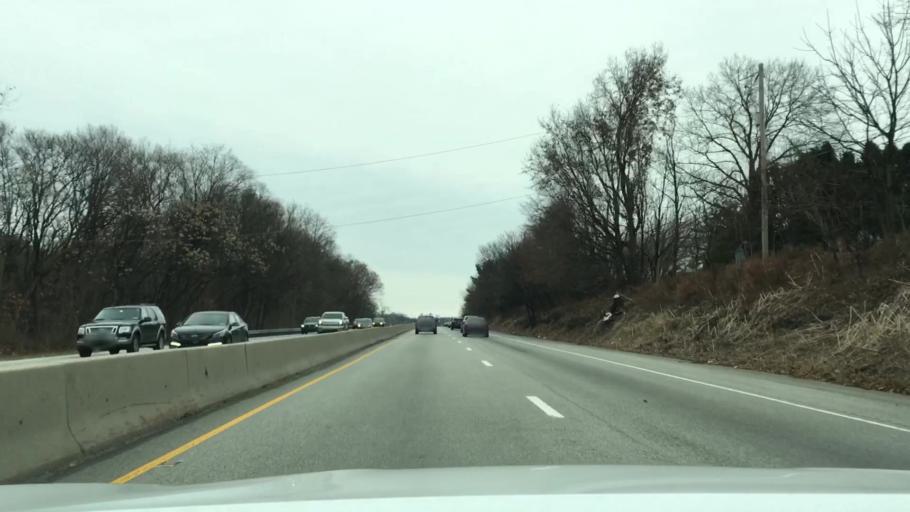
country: US
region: Pennsylvania
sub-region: Montgomery County
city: Pottstown
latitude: 40.2591
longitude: -75.6550
